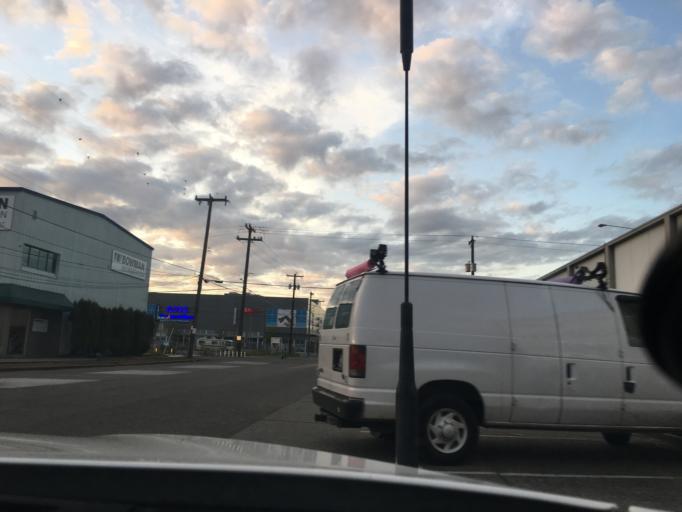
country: US
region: Washington
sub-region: King County
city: Seattle
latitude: 47.6609
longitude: -122.3735
